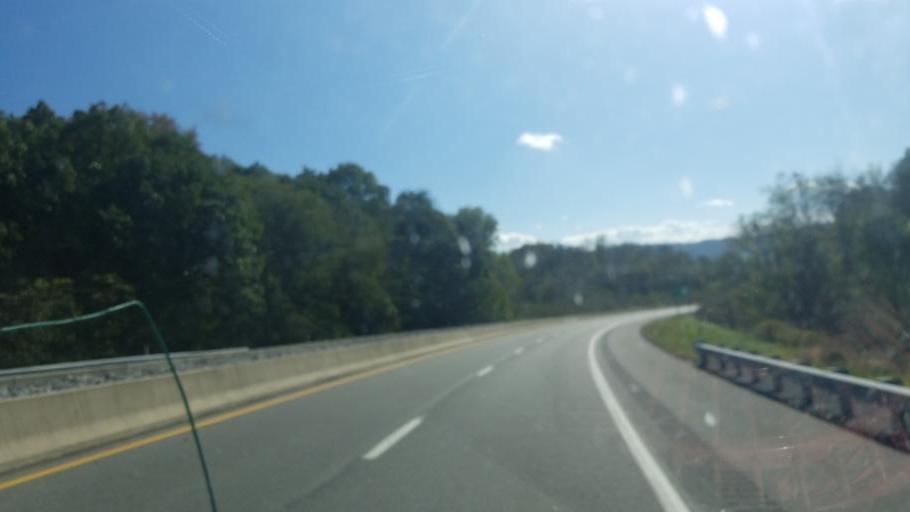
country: US
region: Pennsylvania
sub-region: Bedford County
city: Bedford
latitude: 40.0349
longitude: -78.5191
